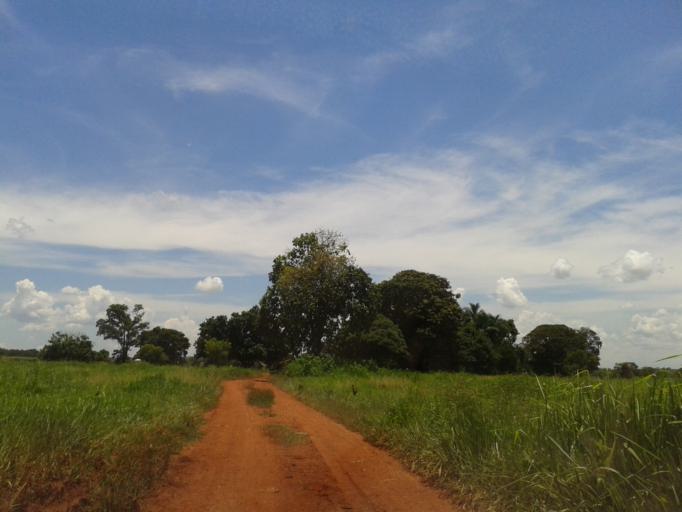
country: BR
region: Minas Gerais
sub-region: Santa Vitoria
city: Santa Vitoria
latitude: -19.1301
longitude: -50.5596
